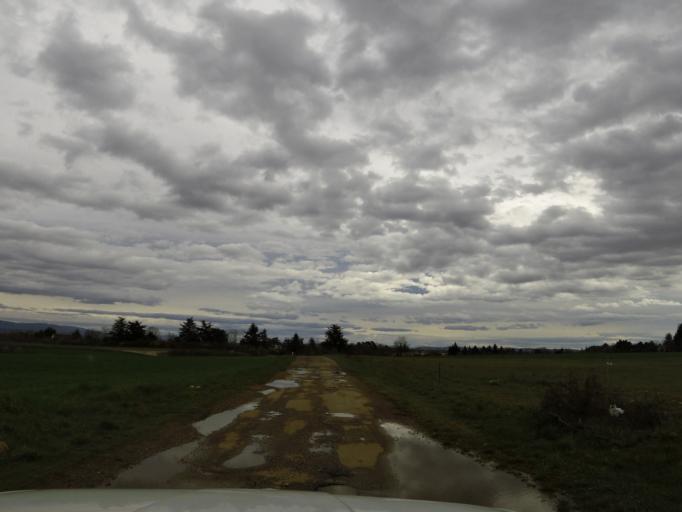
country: FR
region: Rhone-Alpes
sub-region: Departement de l'Ain
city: Meximieux
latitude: 45.8915
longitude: 5.2188
